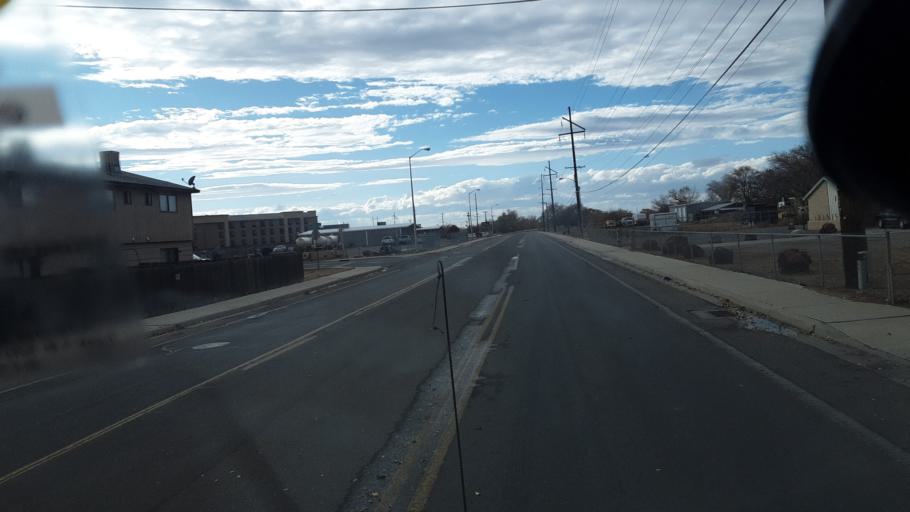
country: US
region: New Mexico
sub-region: San Juan County
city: Farmington
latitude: 36.7267
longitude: -108.1853
